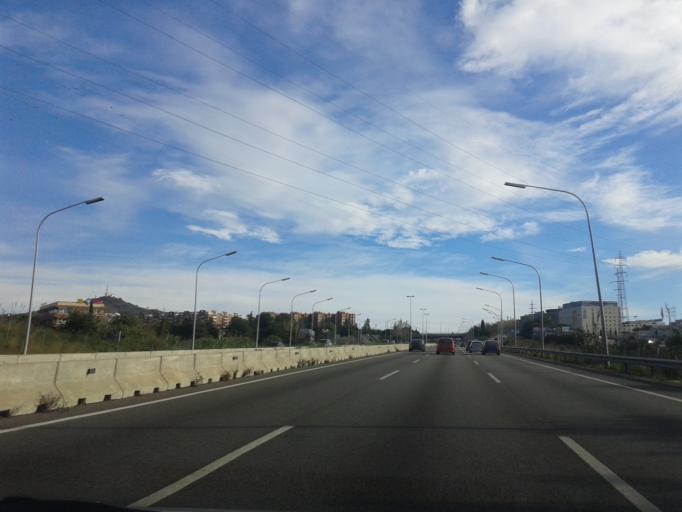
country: ES
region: Catalonia
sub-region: Provincia de Barcelona
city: Sant Joan Despi
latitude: 41.3753
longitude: 2.0659
